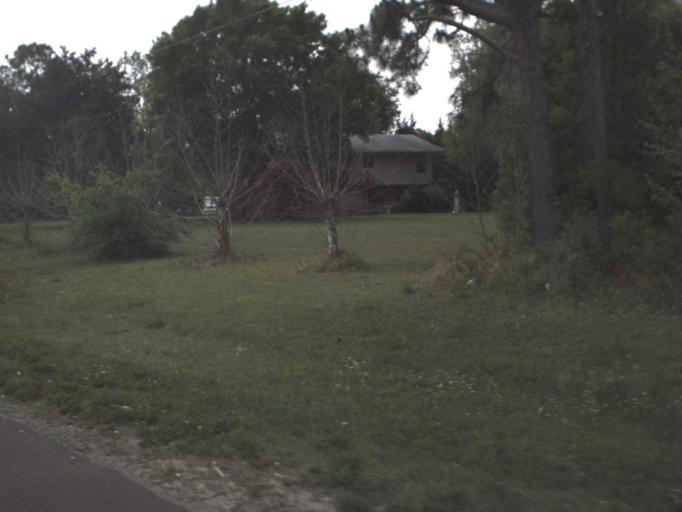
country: US
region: Florida
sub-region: Lake County
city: Mount Dora
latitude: 28.8447
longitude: -81.6338
